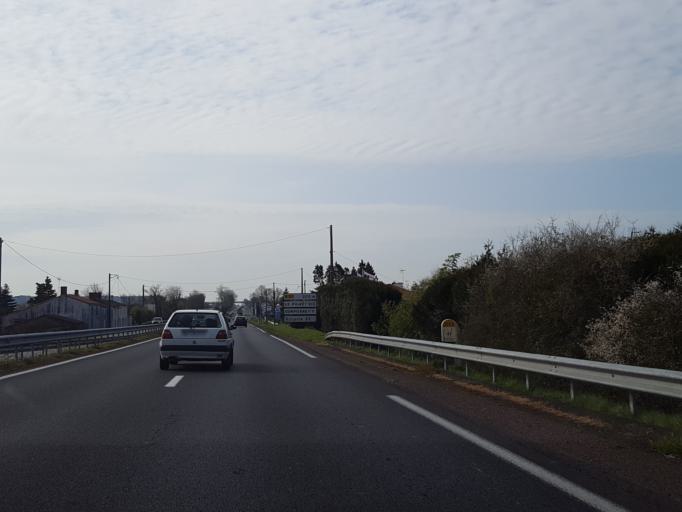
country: FR
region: Pays de la Loire
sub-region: Departement de la Vendee
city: Belleville-sur-Vie
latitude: 46.7536
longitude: -1.4307
